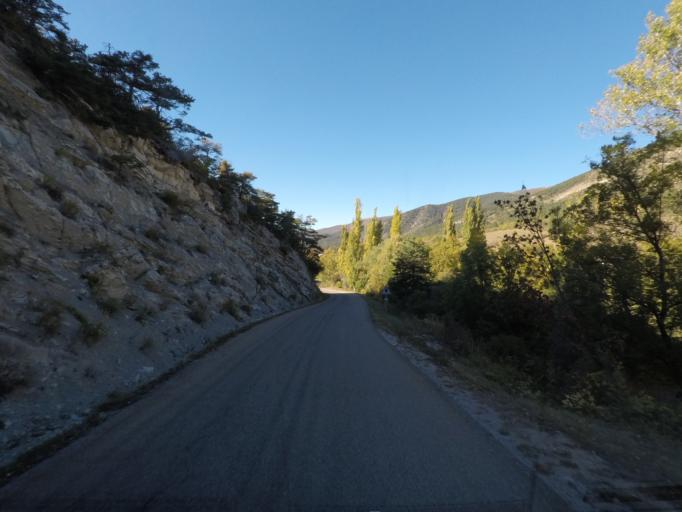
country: FR
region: Provence-Alpes-Cote d'Azur
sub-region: Departement des Hautes-Alpes
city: Serres
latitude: 44.4425
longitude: 5.5554
